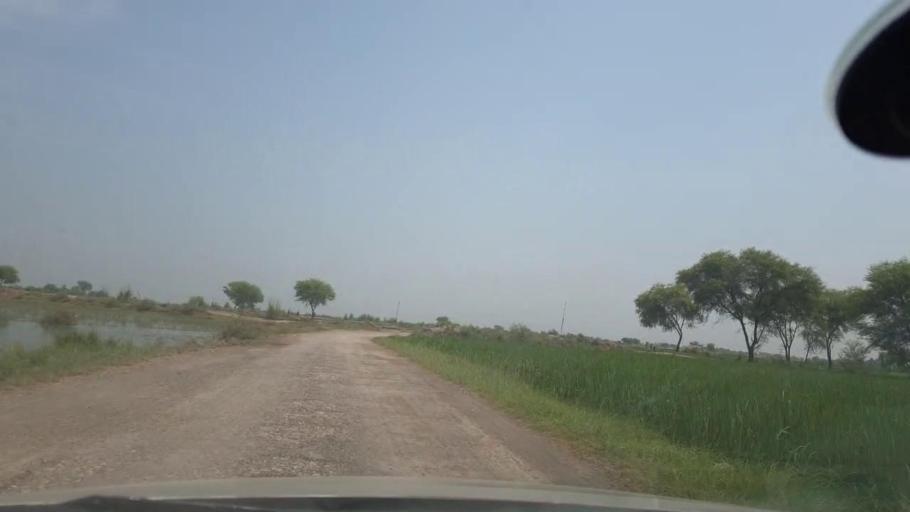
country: PK
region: Sindh
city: Jacobabad
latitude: 28.1371
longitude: 68.3737
